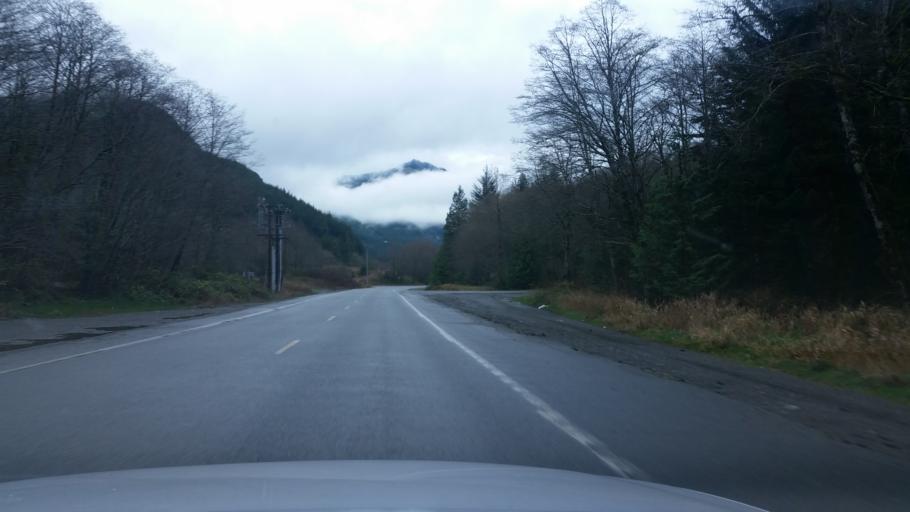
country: US
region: Washington
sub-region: King County
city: Tanner
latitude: 47.4305
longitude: -121.6391
